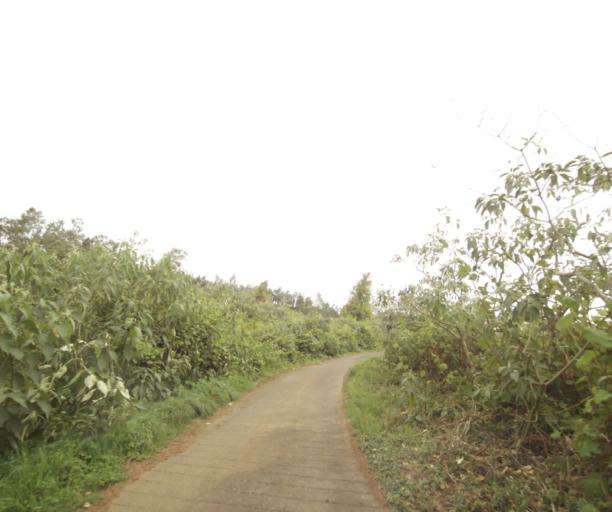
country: RE
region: Reunion
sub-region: Reunion
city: Saint-Paul
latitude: -21.0128
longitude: 55.3531
